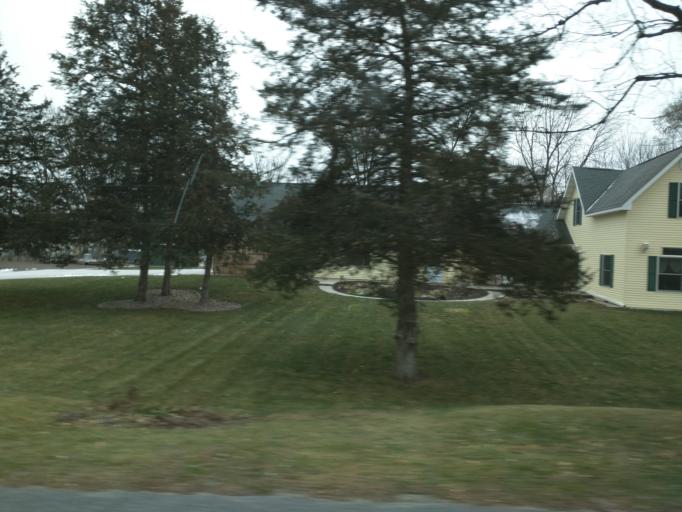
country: US
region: Wisconsin
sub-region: La Crosse County
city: French Island
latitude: 43.8612
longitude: -91.2698
